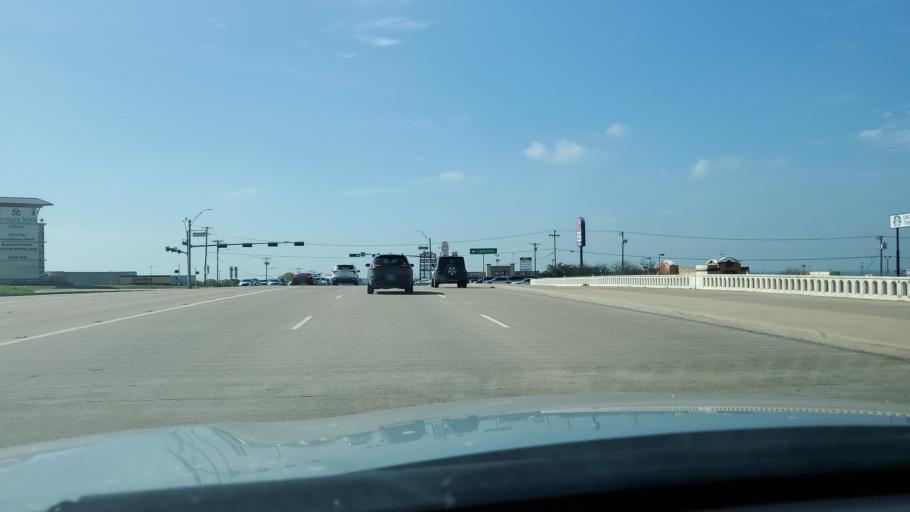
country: US
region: Texas
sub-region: Bell County
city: Temple
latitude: 31.0735
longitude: -97.3680
